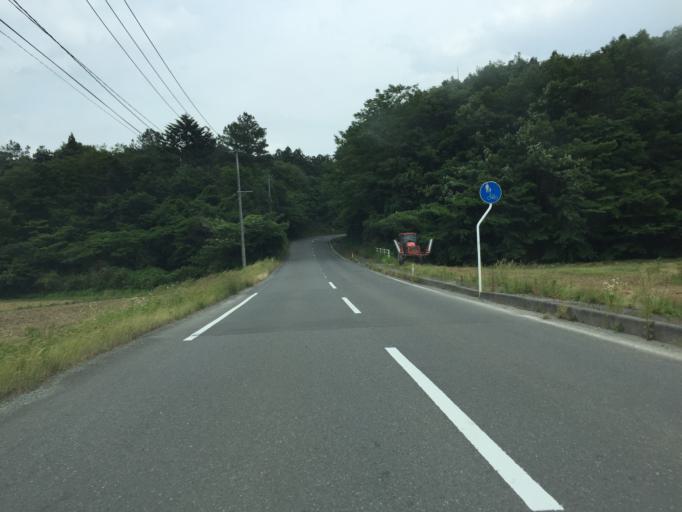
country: JP
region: Miyagi
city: Marumori
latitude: 37.8655
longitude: 140.8901
